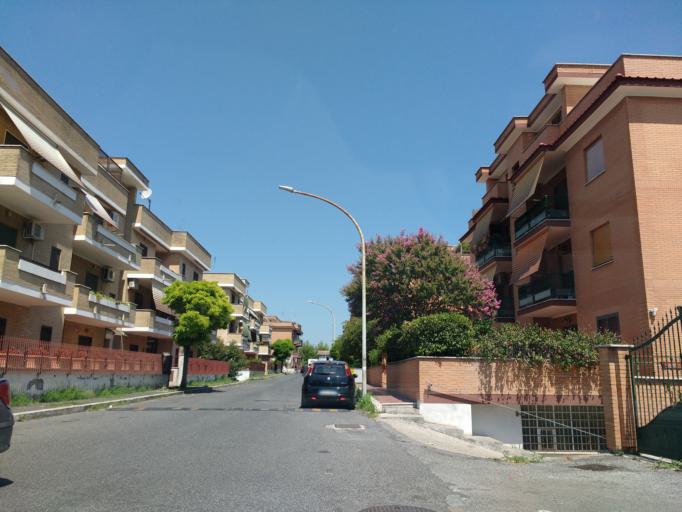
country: IT
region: Latium
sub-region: Citta metropolitana di Roma Capitale
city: Villa Adriana
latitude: 41.9549
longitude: 12.7712
